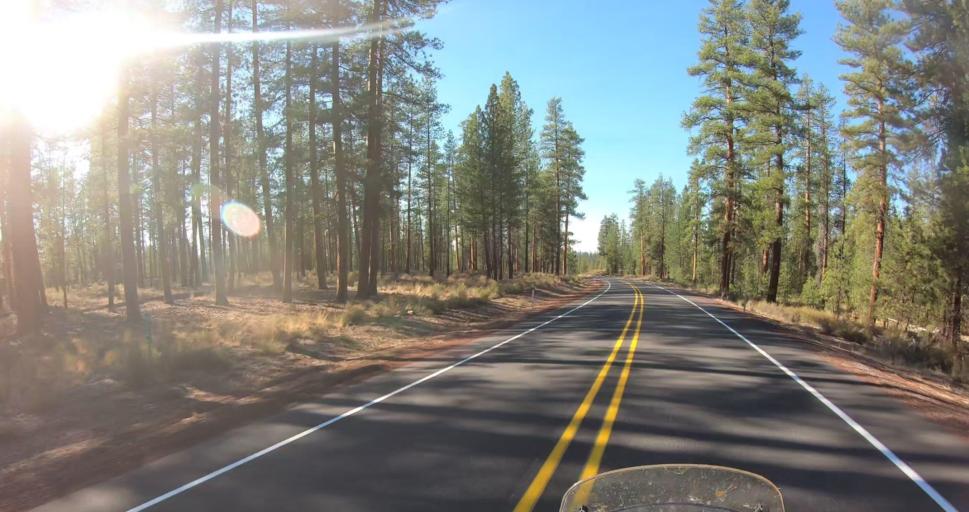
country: US
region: Oregon
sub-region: Deschutes County
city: La Pine
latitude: 43.4721
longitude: -121.4013
